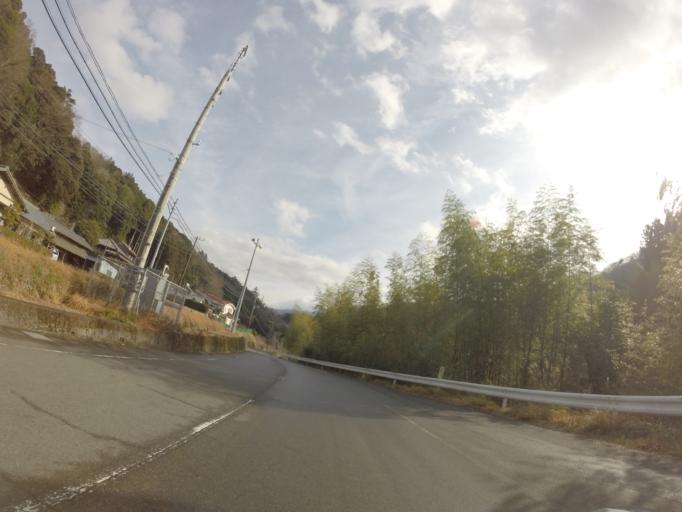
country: JP
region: Shizuoka
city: Heda
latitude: 34.8857
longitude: 138.9025
